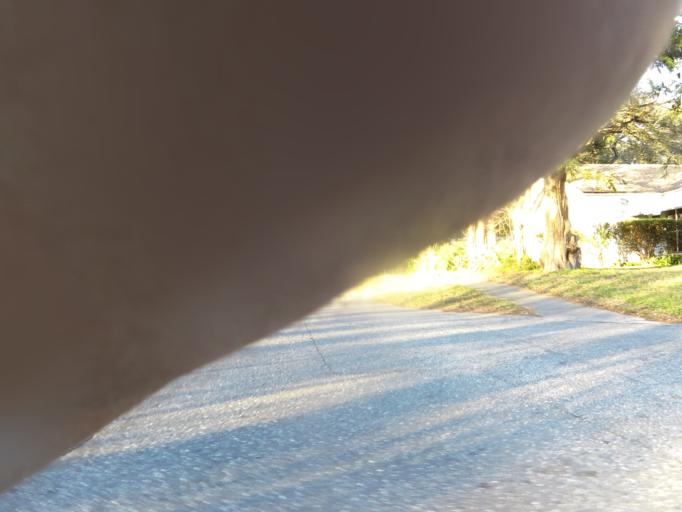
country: US
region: Florida
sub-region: Duval County
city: Jacksonville
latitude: 30.3176
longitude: -81.7201
